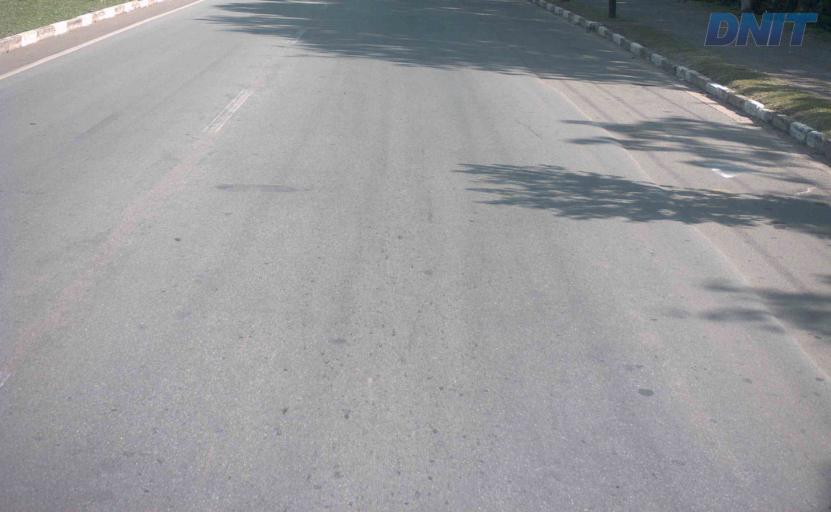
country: BR
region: Minas Gerais
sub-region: Ipatinga
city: Ipatinga
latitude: -19.4670
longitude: -42.5364
